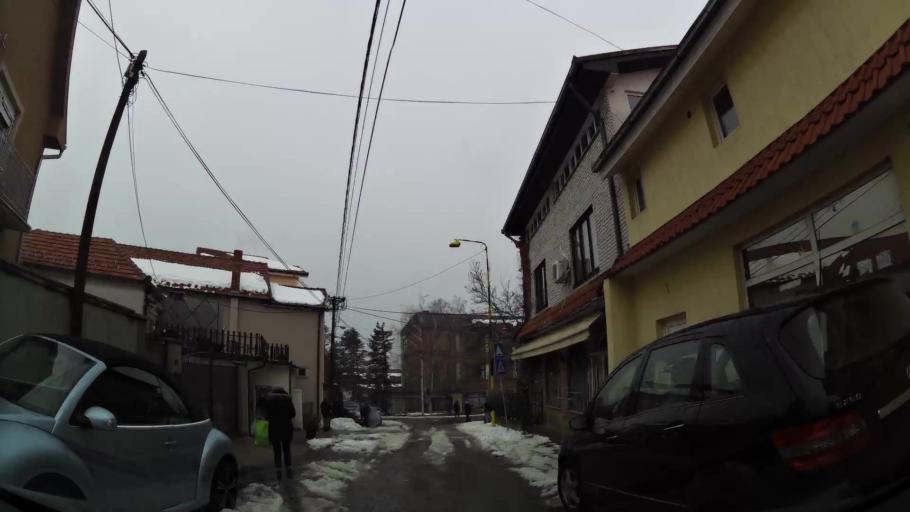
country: RS
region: Central Serbia
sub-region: Belgrade
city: Zvezdara
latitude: 44.7582
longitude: 20.5292
